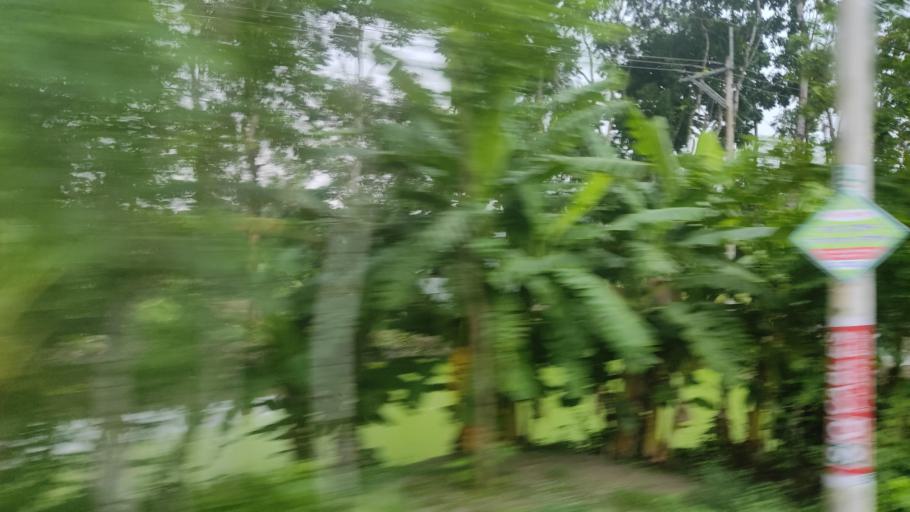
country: BD
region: Barisal
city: Bhandaria
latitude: 22.3026
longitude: 90.3244
